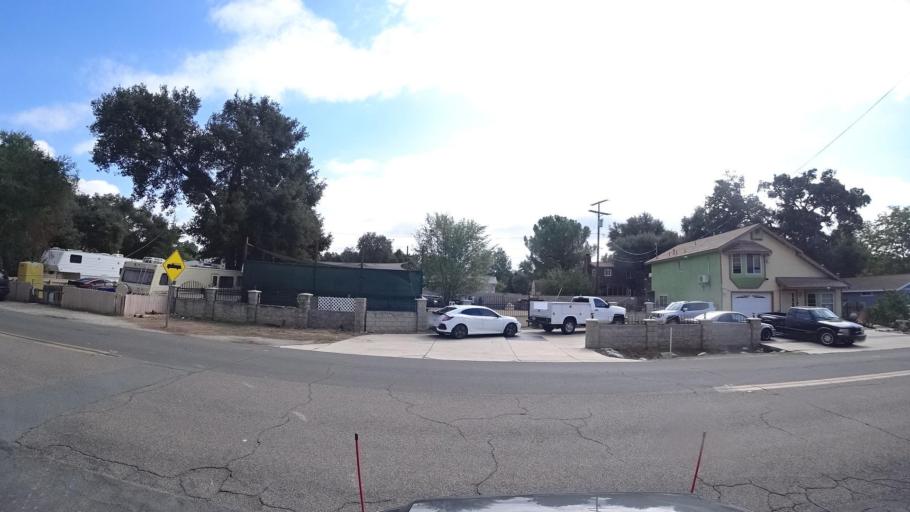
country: US
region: California
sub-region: San Diego County
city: Campo
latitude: 32.6792
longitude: -116.5092
